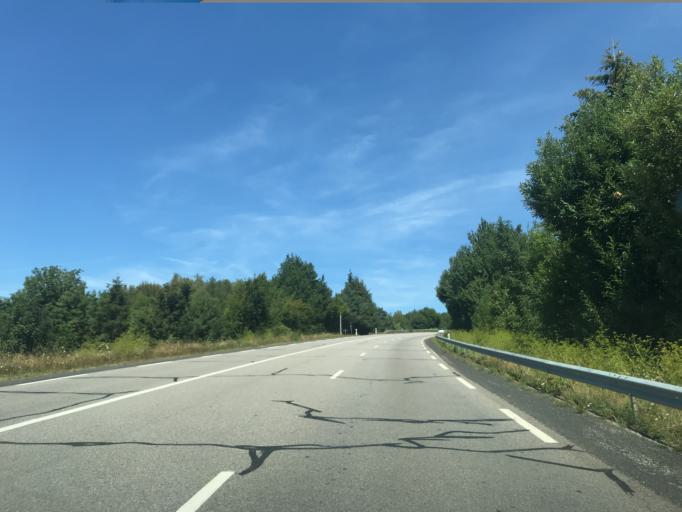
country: FR
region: Limousin
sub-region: Departement de la Correze
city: Naves
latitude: 45.3001
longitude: 1.8150
